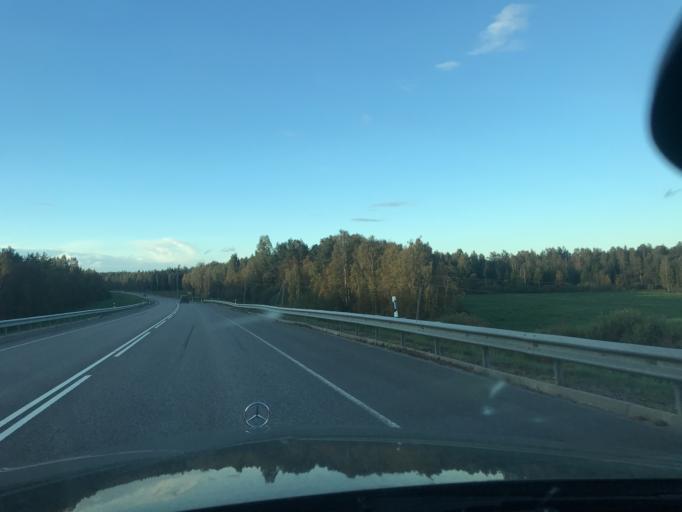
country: EE
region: Vorumaa
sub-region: Voru linn
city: Voru
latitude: 57.8283
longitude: 27.0632
